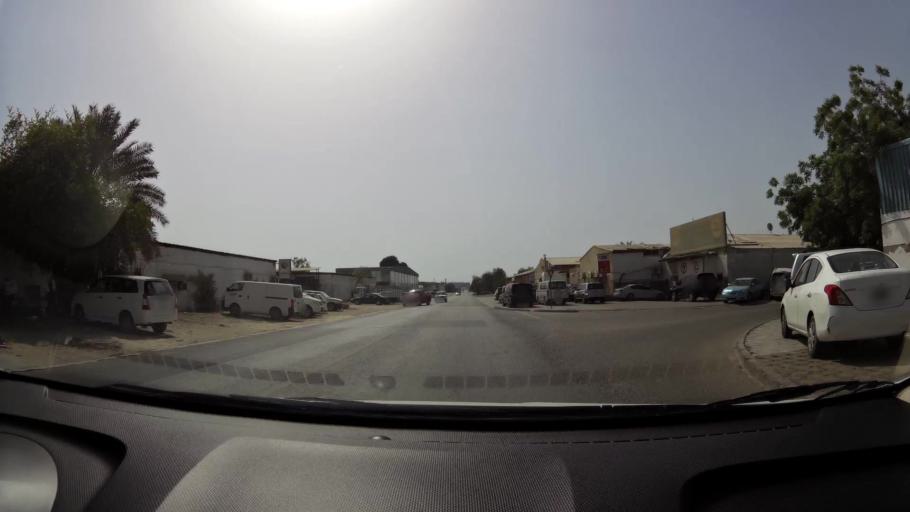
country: AE
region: Ash Shariqah
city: Sharjah
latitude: 25.2307
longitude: 55.3717
